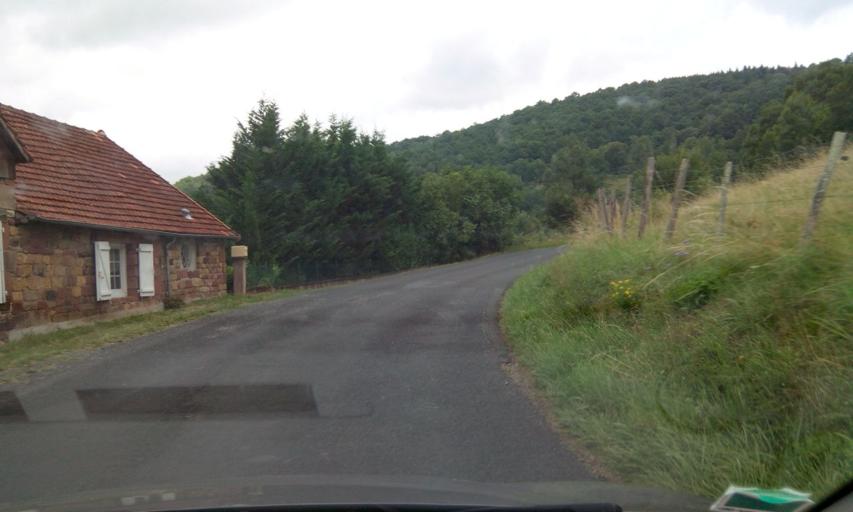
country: FR
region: Limousin
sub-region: Departement de la Correze
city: Meyssac
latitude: 45.0657
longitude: 1.6368
